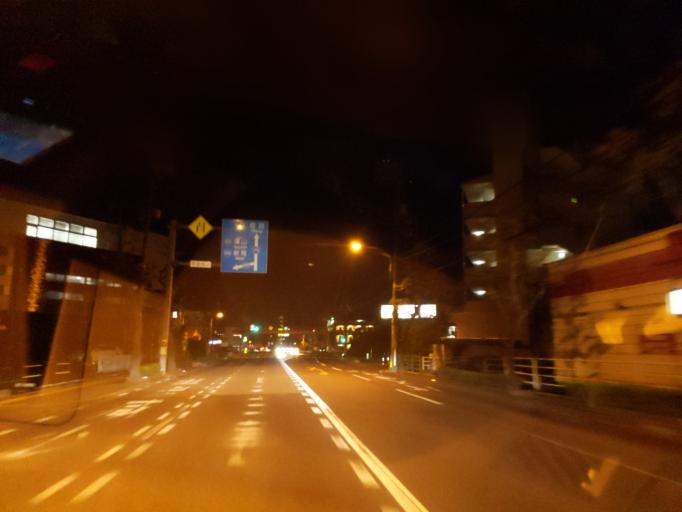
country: JP
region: Okayama
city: Okayama-shi
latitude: 34.6686
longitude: 133.9503
